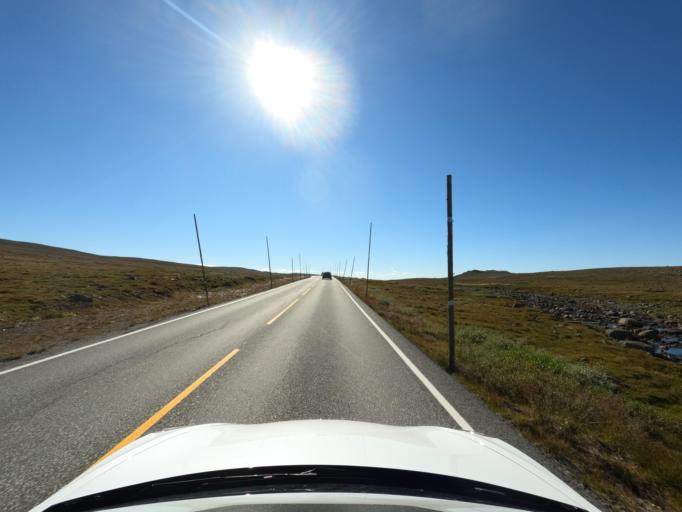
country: NO
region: Hordaland
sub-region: Eidfjord
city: Eidfjord
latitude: 60.3882
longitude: 7.5919
